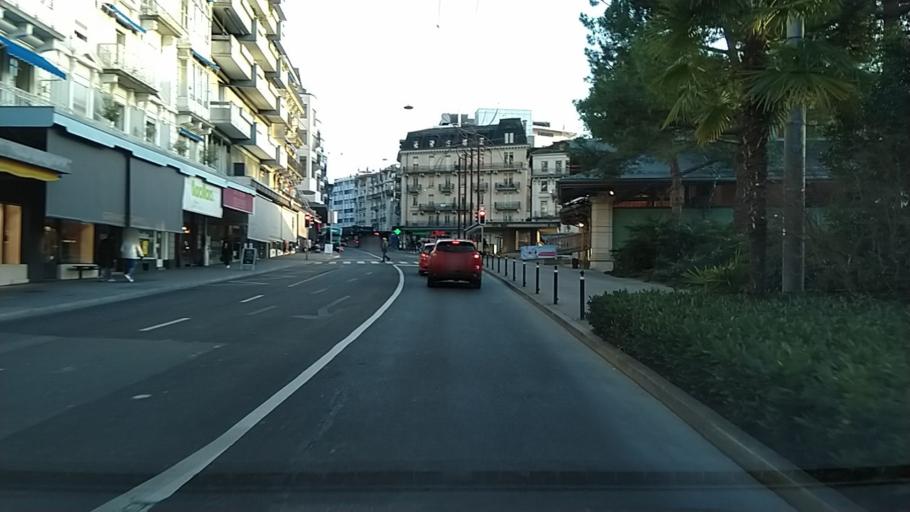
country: CH
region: Vaud
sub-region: Riviera-Pays-d'Enhaut District
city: Montreux
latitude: 46.4328
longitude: 6.9102
